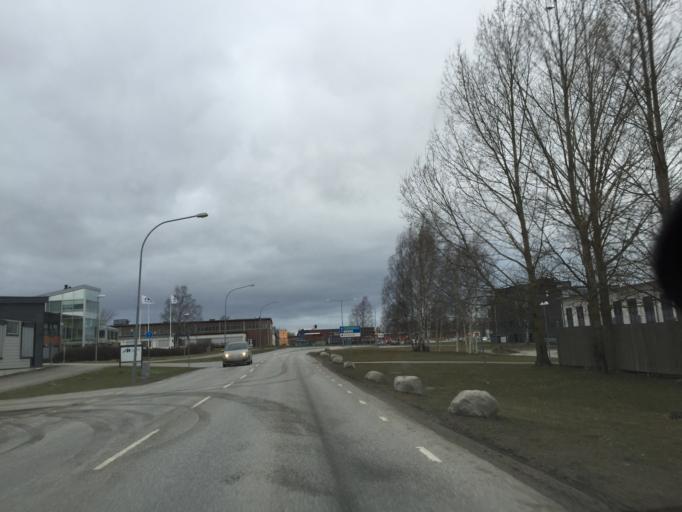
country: SE
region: OErebro
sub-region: Orebro Kommun
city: Orebro
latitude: 59.2573
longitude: 15.1794
